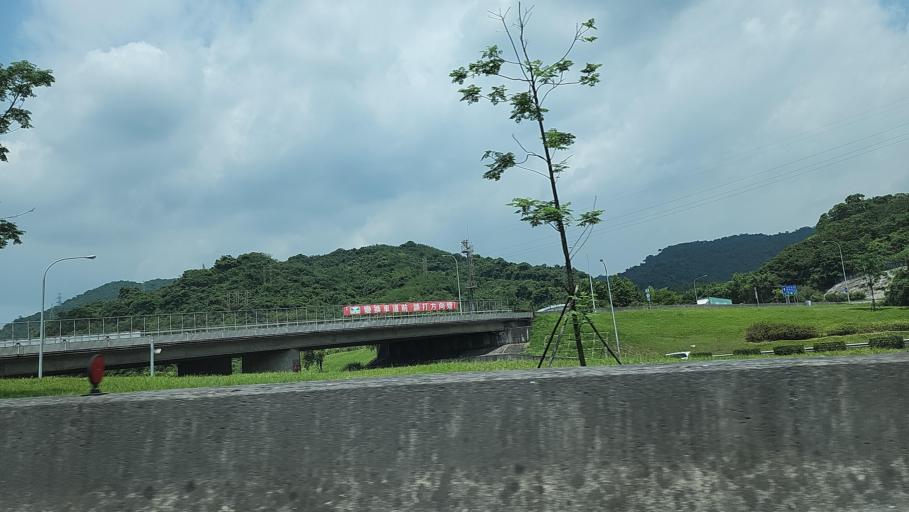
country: TW
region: Taiwan
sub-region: Keelung
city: Keelung
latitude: 25.0864
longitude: 121.6875
